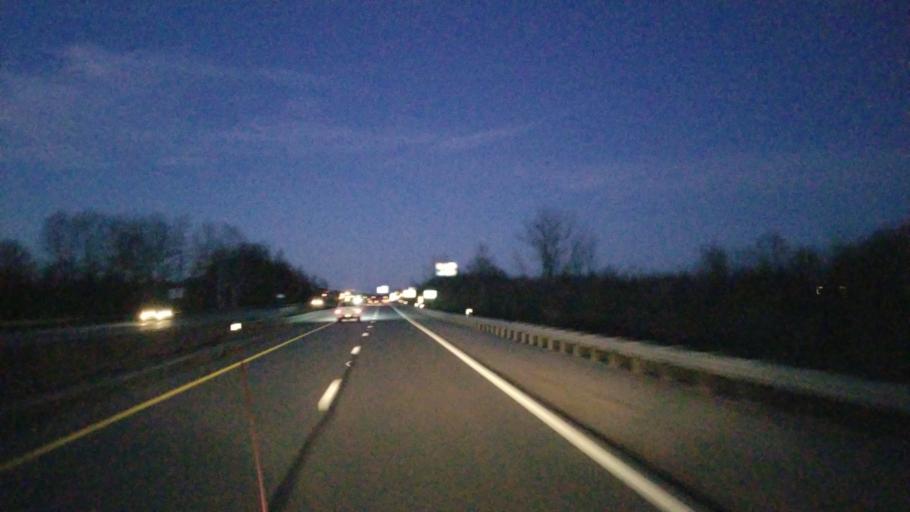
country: US
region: West Virginia
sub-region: Wood County
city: Mineral Wells
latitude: 39.1654
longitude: -81.5407
